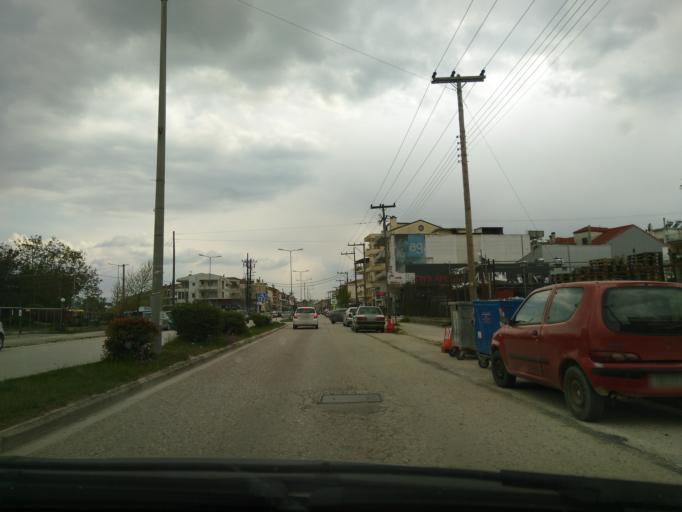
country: GR
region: Epirus
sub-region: Nomos Ioanninon
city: Ioannina
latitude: 39.6618
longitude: 20.8586
